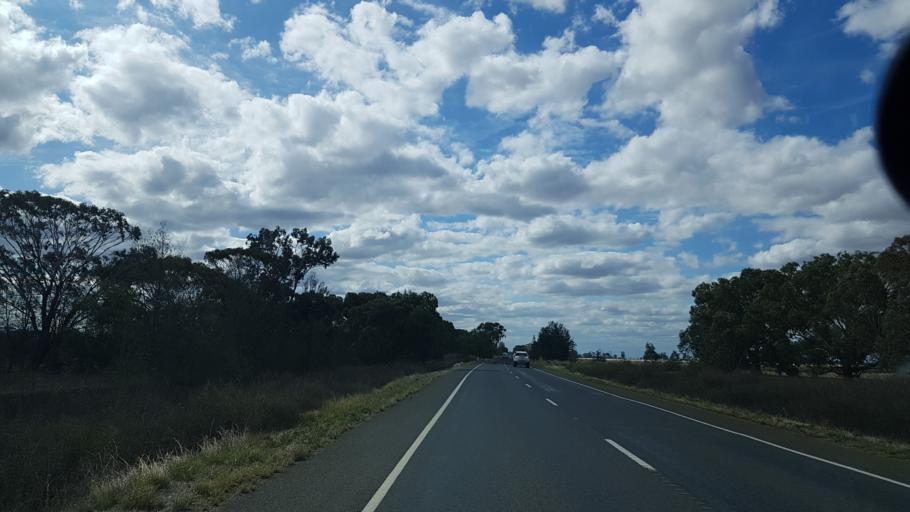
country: AU
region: Victoria
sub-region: Swan Hill
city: Swan Hill
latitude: -35.9883
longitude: 143.9460
